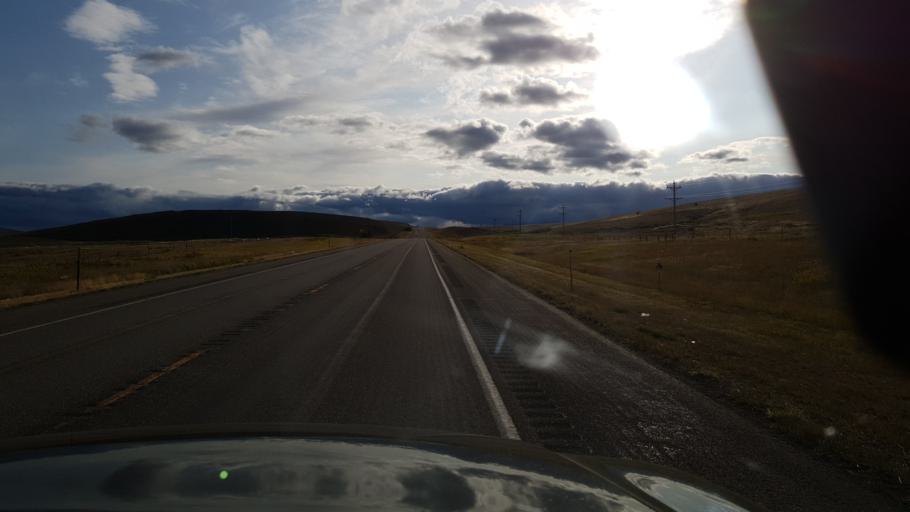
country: US
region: Montana
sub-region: Glacier County
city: South Browning
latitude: 48.5241
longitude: -113.0680
